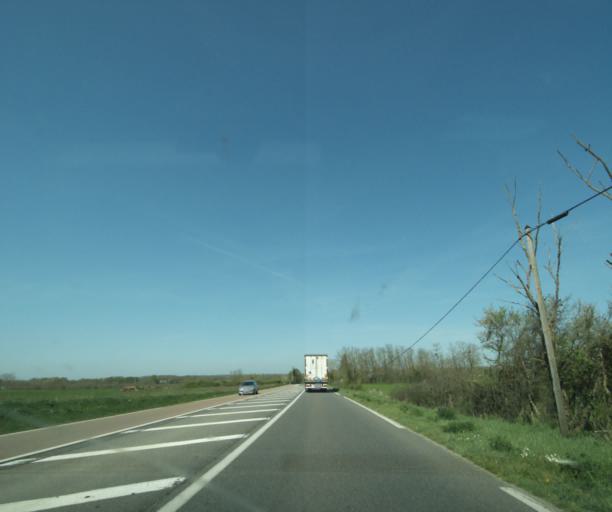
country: FR
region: Bourgogne
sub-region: Departement de la Nievre
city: Chantenay-Saint-Imbert
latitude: 46.7405
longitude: 3.1598
